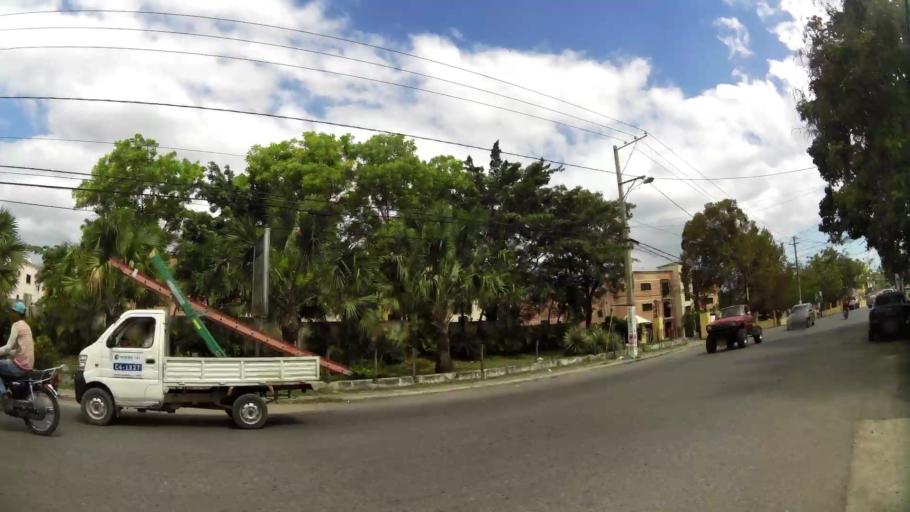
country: DO
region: San Cristobal
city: San Cristobal
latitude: 18.4142
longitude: -70.1177
